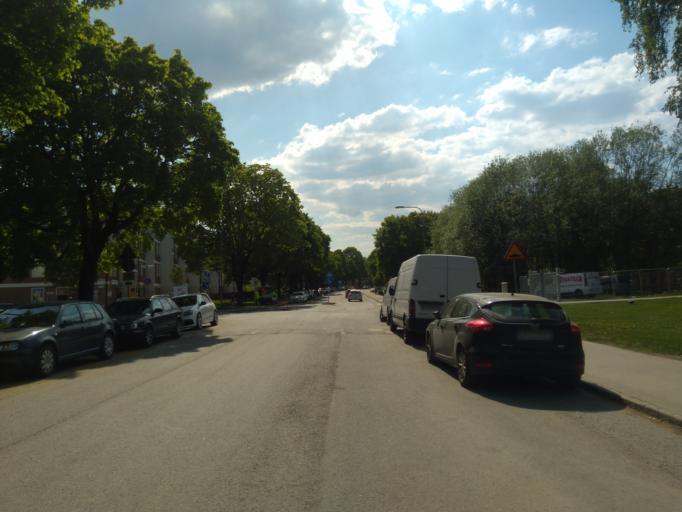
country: SE
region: Stockholm
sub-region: Stockholms Kommun
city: Arsta
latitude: 59.2559
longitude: 18.0786
